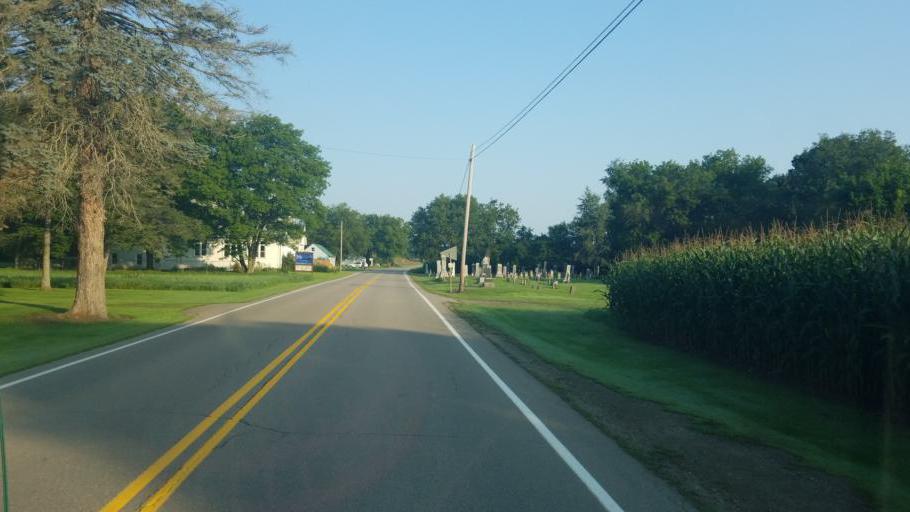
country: US
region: Pennsylvania
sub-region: Tioga County
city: Westfield
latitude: 41.9947
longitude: -77.4972
